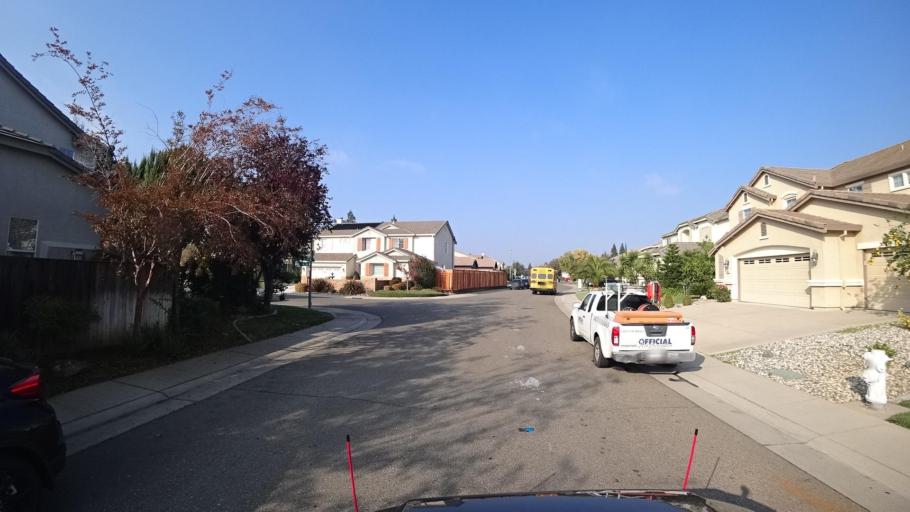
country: US
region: California
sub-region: Sacramento County
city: Elk Grove
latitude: 38.4113
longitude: -121.3410
